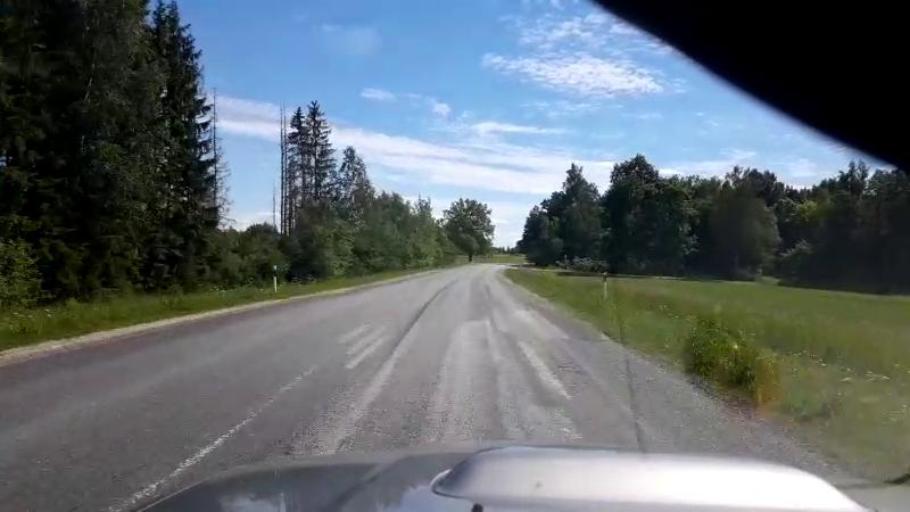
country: EE
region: Laeaene-Virumaa
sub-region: Rakke vald
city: Rakke
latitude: 58.8812
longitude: 26.2941
